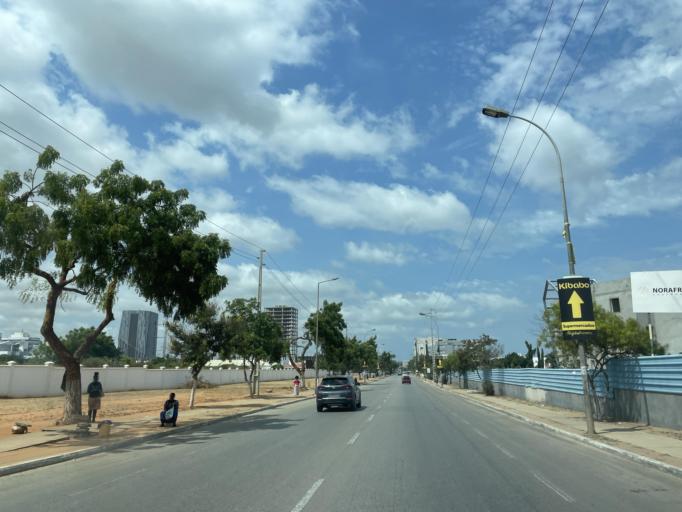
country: AO
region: Luanda
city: Luanda
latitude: -8.9162
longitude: 13.1908
